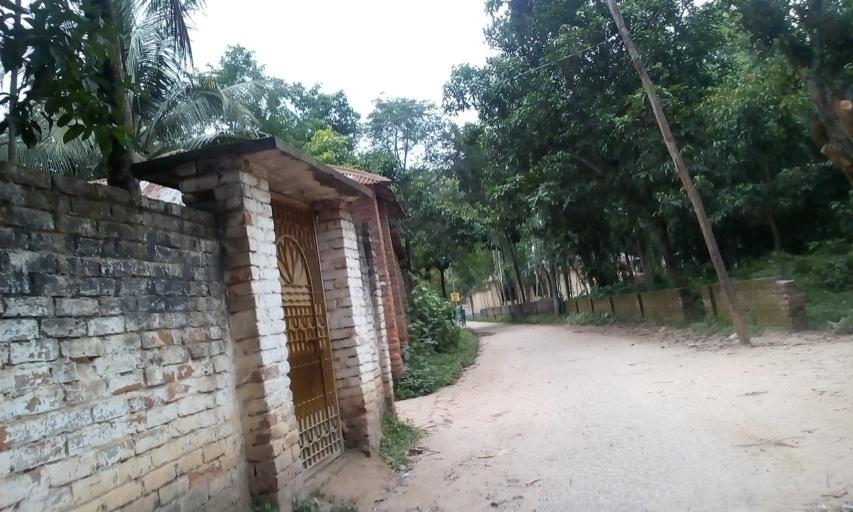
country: IN
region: West Bengal
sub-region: Dakshin Dinajpur
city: Balurghat
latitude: 25.3948
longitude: 88.9863
